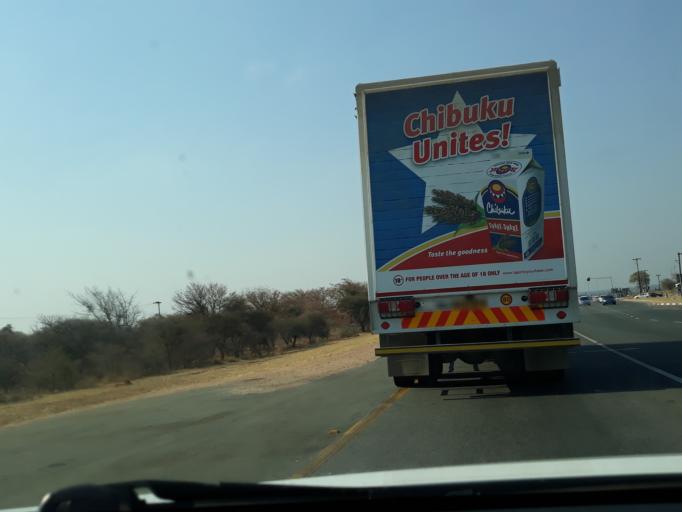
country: BW
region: Central
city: Tonota
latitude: -21.4248
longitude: 27.4417
